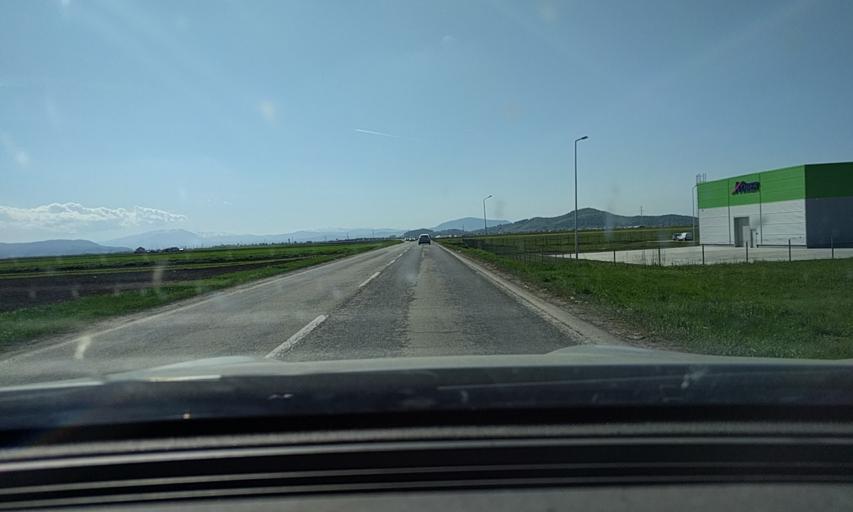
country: RO
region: Brasov
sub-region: Comuna Prejmer
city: Prejmer
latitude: 45.7144
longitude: 25.7338
